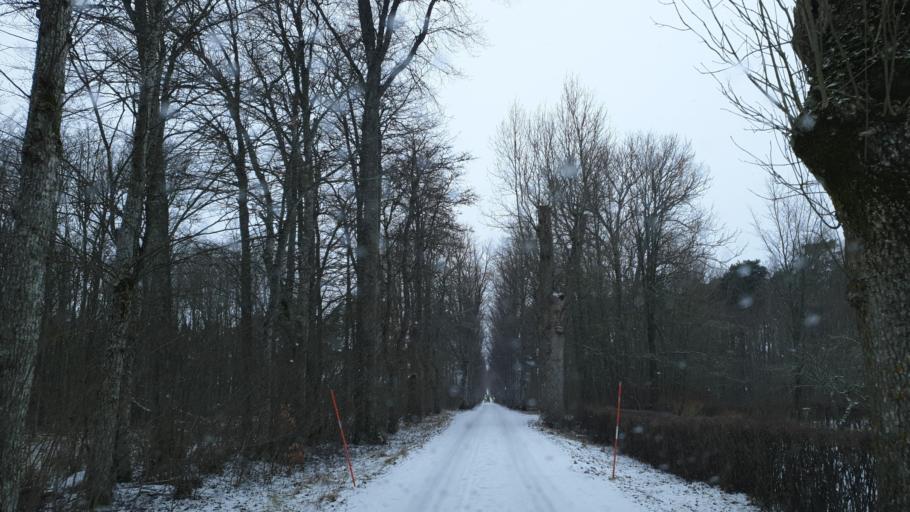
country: SE
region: Gotland
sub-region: Gotland
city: Visby
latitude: 57.5234
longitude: 18.4489
